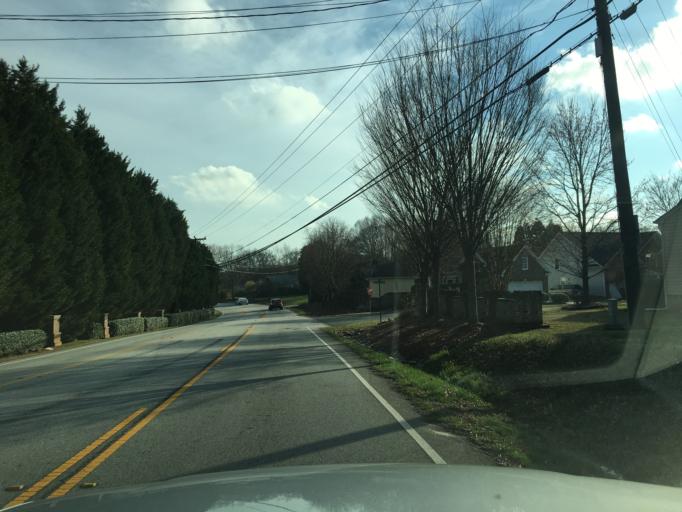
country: US
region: South Carolina
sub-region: Greenville County
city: Taylors
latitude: 34.8898
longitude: -82.2903
